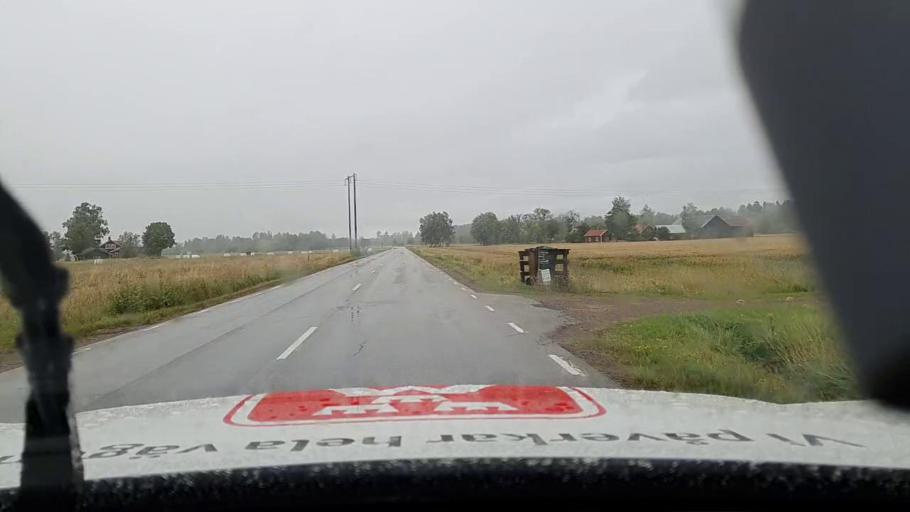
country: SE
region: Vaestra Goetaland
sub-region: Toreboda Kommun
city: Toereboda
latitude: 58.6930
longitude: 14.1299
